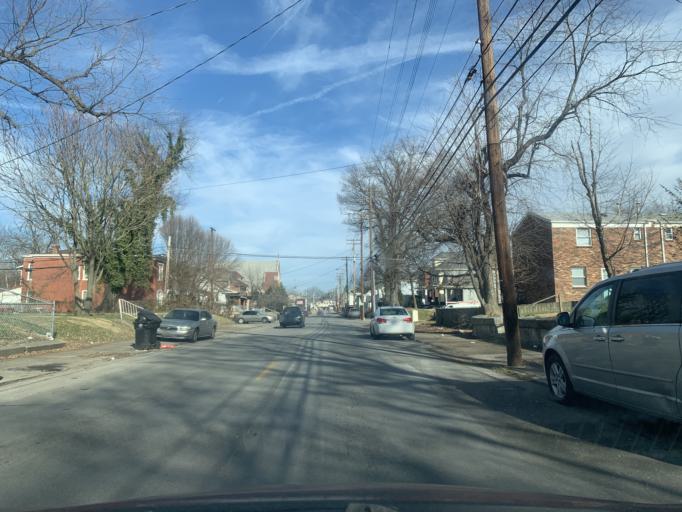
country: US
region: Kentucky
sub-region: Jefferson County
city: Louisville
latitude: 38.2676
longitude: -85.7920
